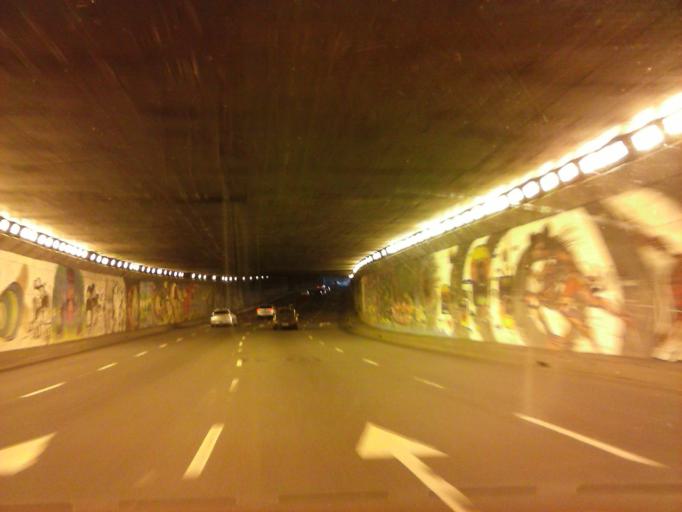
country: BR
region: Rio Grande do Sul
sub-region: Porto Alegre
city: Porto Alegre
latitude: -30.0310
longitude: -51.2190
